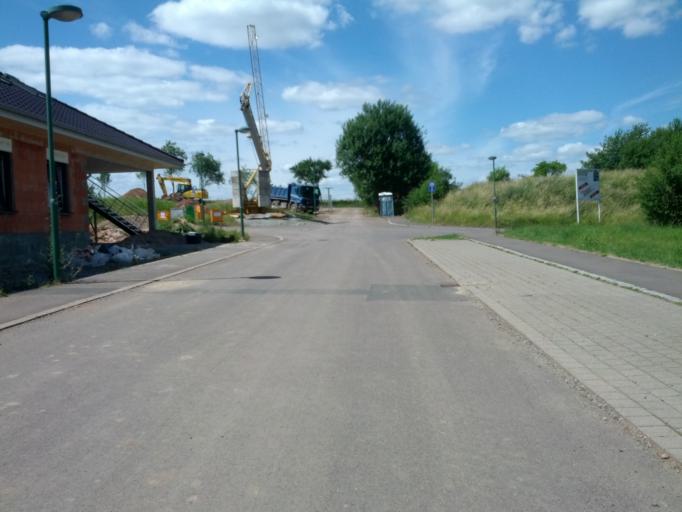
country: DE
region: Thuringia
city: Bischofroda
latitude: 51.0070
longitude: 10.3568
